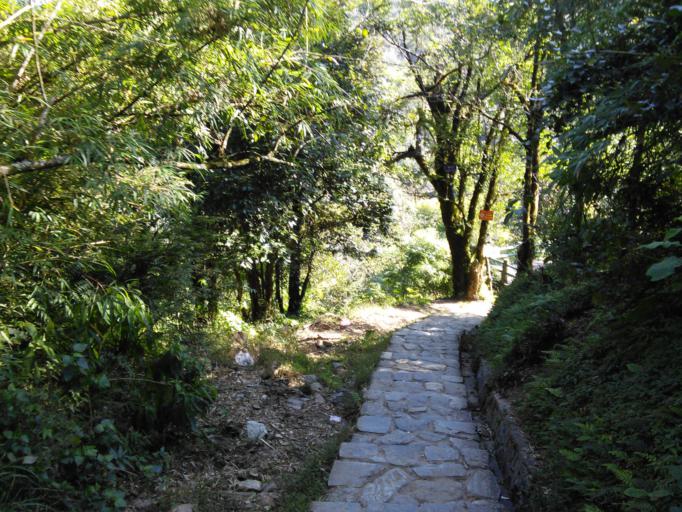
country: VN
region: Lao Cai
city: Sa Pa
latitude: 22.3515
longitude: 103.7734
